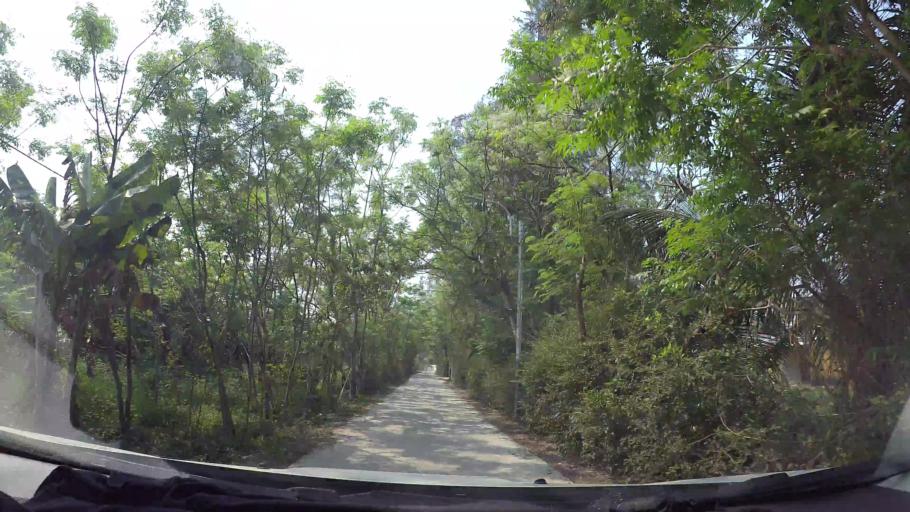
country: VN
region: Da Nang
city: Cam Le
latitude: 15.9750
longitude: 108.2267
